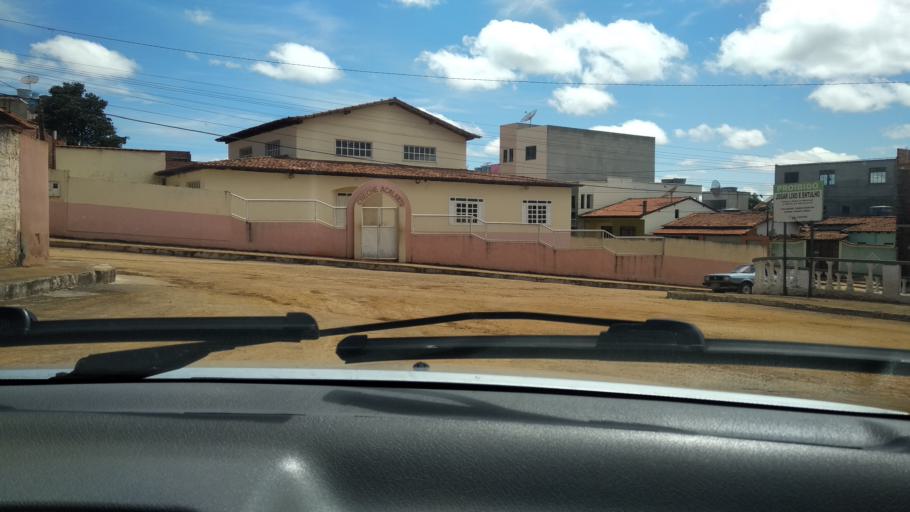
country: BR
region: Bahia
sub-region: Caetite
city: Caetite
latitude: -14.0594
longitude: -42.4823
